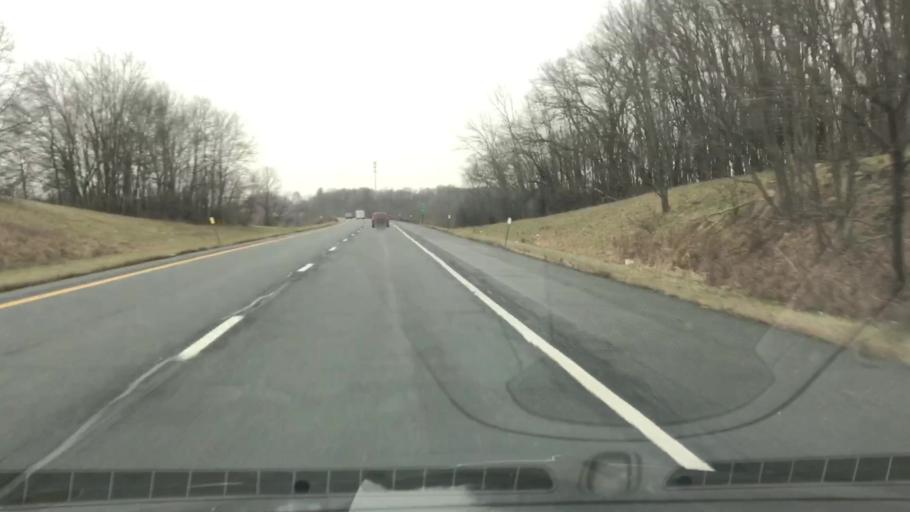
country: US
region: New York
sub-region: Orange County
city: Middletown
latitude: 41.4068
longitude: -74.4852
